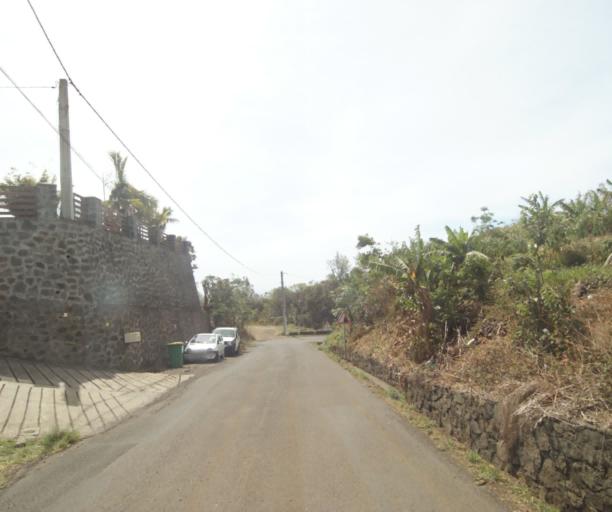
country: RE
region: Reunion
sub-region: Reunion
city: Trois-Bassins
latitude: -21.0693
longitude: 55.2891
